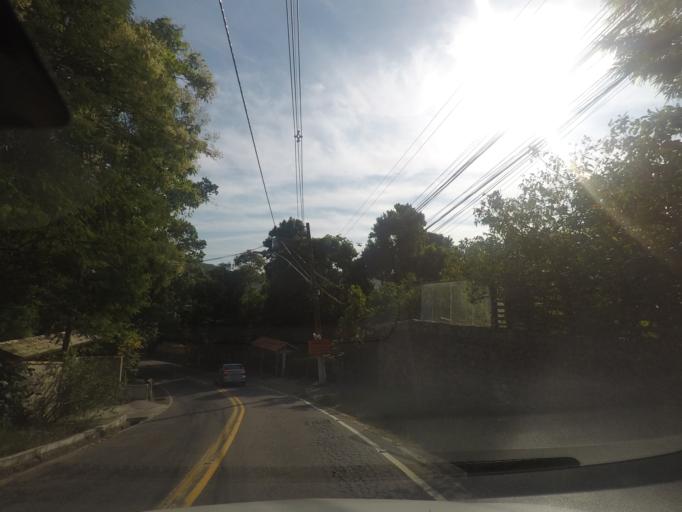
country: BR
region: Rio de Janeiro
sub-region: Niteroi
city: Niteroi
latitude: -22.9654
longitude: -43.0182
